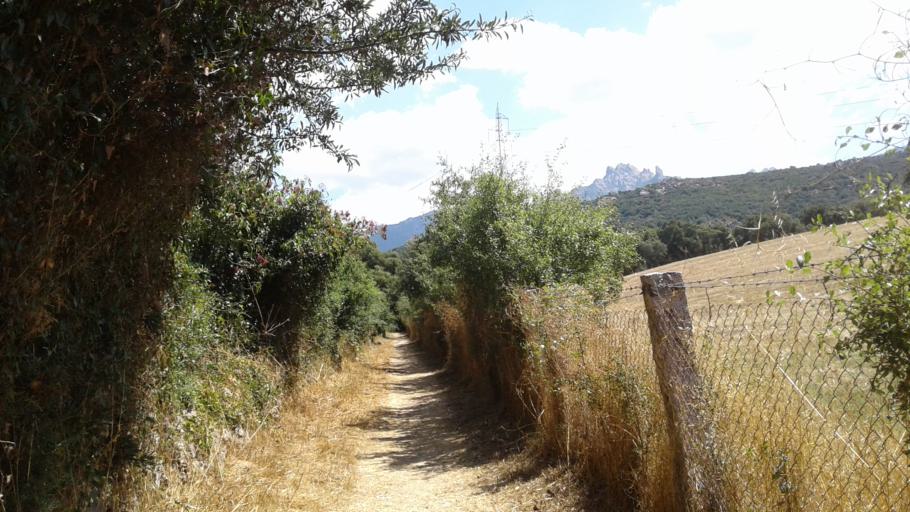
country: IT
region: Sardinia
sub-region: Provincia di Olbia-Tempio
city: Calangianus
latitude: 40.9095
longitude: 9.1713
